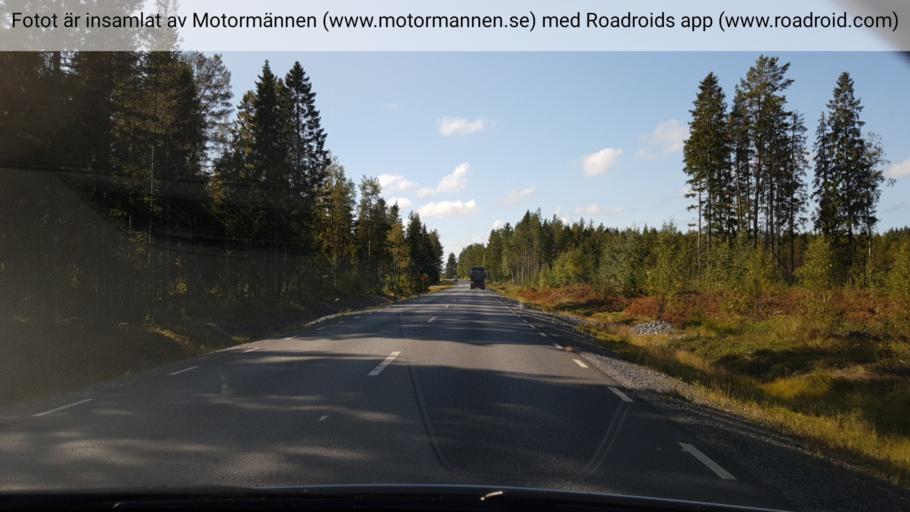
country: SE
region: Vaesterbotten
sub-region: Robertsfors Kommun
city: Robertsfors
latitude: 64.2011
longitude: 20.8553
